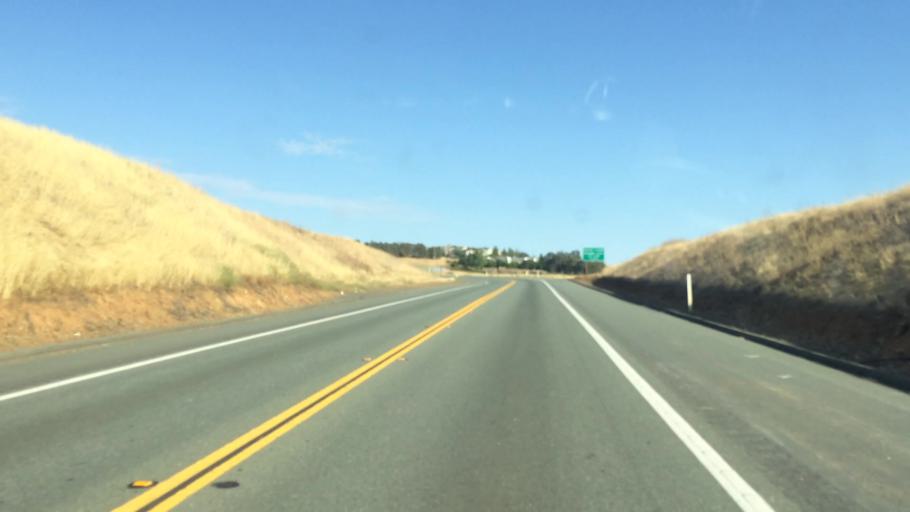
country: US
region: California
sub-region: Amador County
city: Sutter Creek
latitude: 38.3852
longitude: -120.8117
